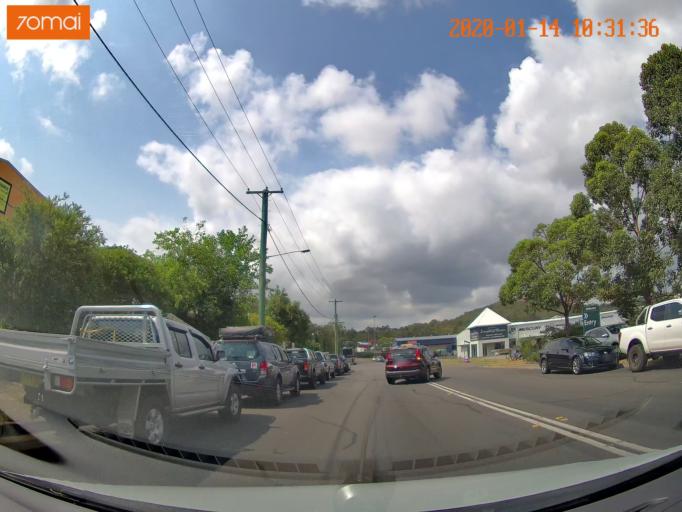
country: AU
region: New South Wales
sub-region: Lake Macquarie Shire
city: Dora Creek
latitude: -33.1198
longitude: 151.4709
